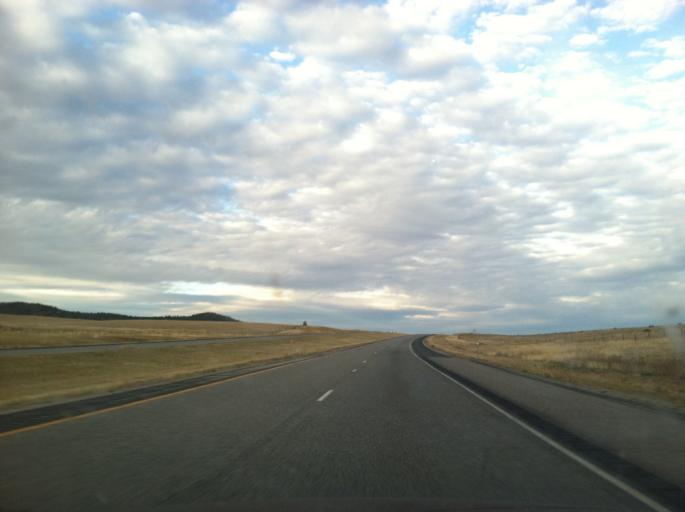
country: US
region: Montana
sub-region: Jefferson County
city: Whitehall
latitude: 45.8808
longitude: -111.8721
